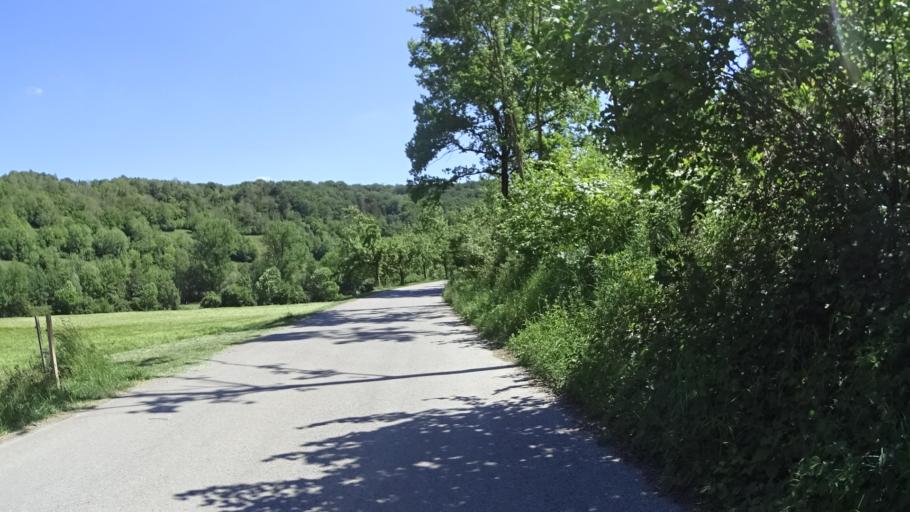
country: DE
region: Bavaria
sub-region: Regierungsbezirk Mittelfranken
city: Adelshofen
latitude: 49.4130
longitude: 10.1514
